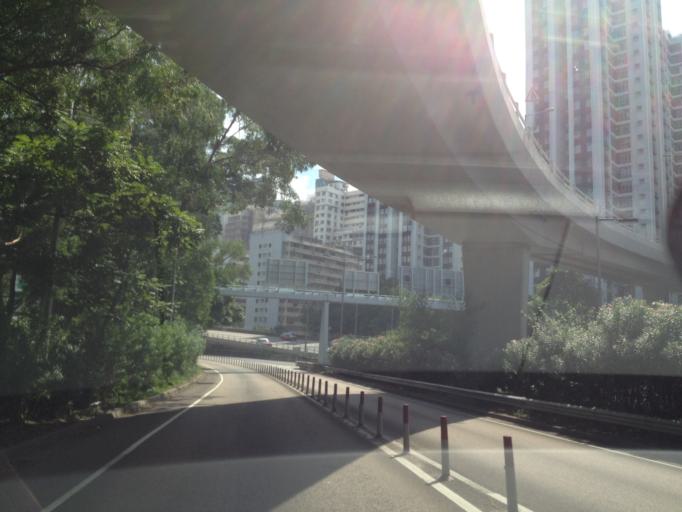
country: HK
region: Kowloon City
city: Kowloon
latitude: 22.2859
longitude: 114.2216
